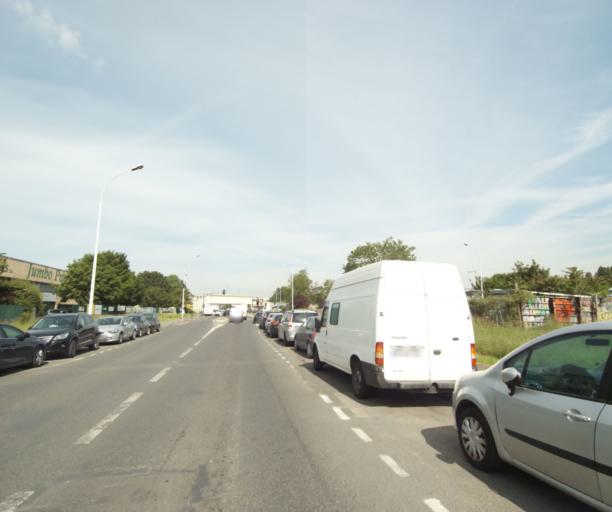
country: FR
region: Ile-de-France
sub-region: Departement des Hauts-de-Seine
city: Villeneuve-la-Garenne
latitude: 48.9285
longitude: 2.3116
